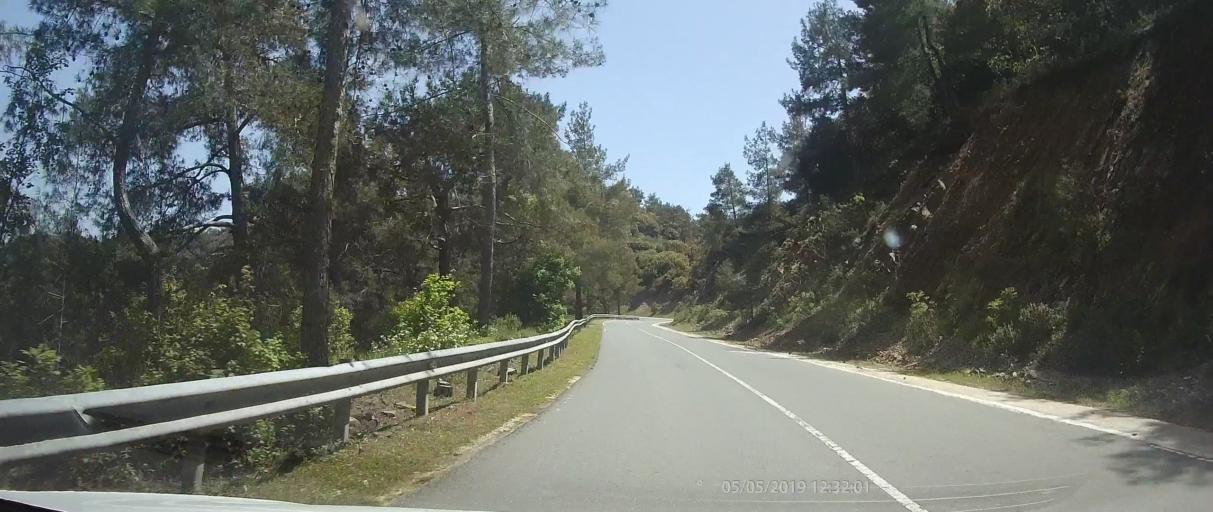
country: CY
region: Lefkosia
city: Kakopetria
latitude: 34.9820
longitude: 32.7539
